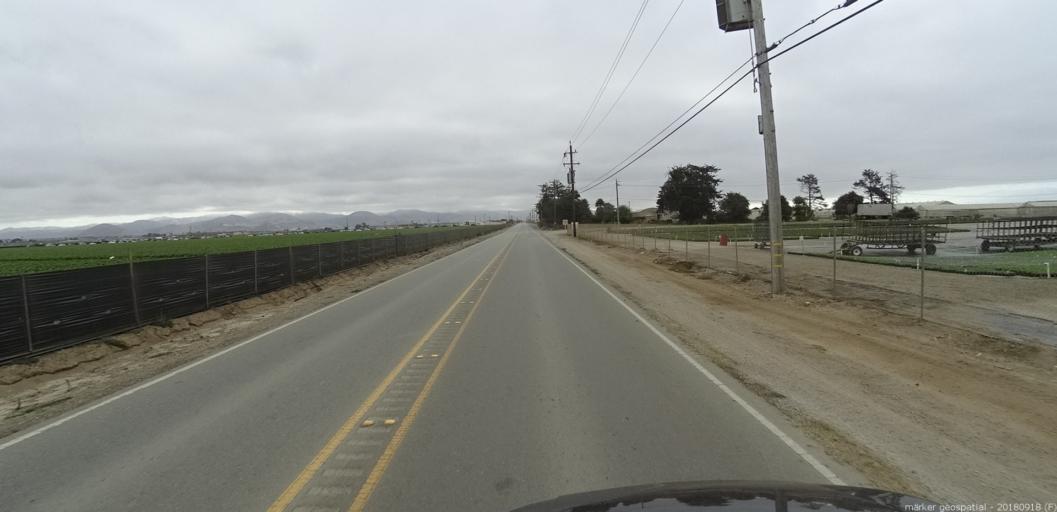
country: US
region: California
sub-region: Monterey County
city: Prunedale
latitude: 36.7407
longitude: -121.6785
